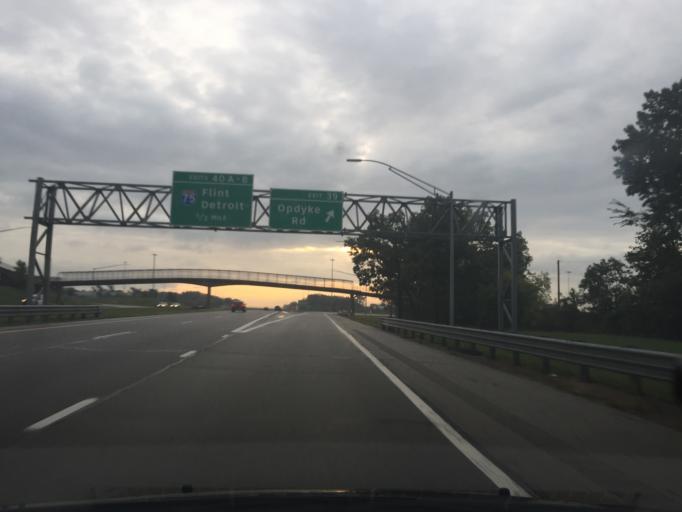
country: US
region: Michigan
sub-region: Oakland County
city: Pontiac
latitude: 42.6419
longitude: -83.2567
